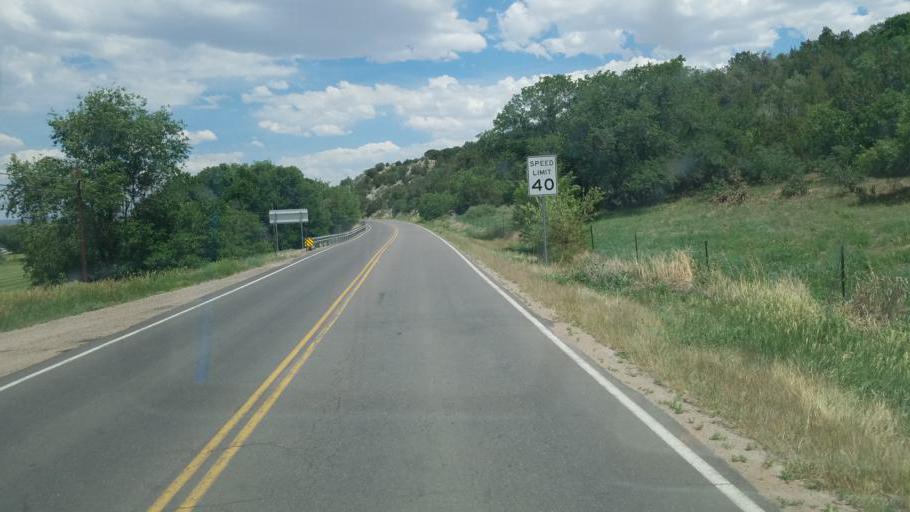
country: US
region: Colorado
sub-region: Fremont County
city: Florence
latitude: 38.4054
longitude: -105.1624
